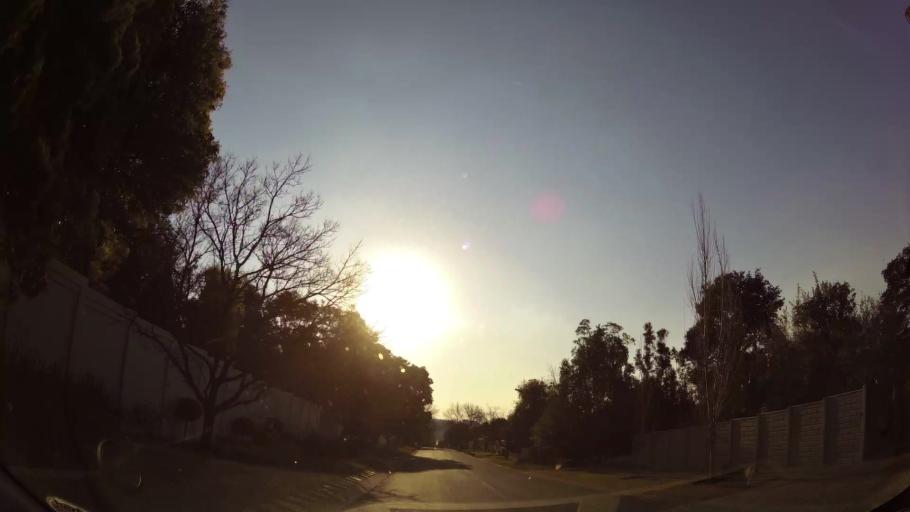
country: ZA
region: Gauteng
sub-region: City of Johannesburg Metropolitan Municipality
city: Diepsloot
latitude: -26.0622
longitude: 27.9880
